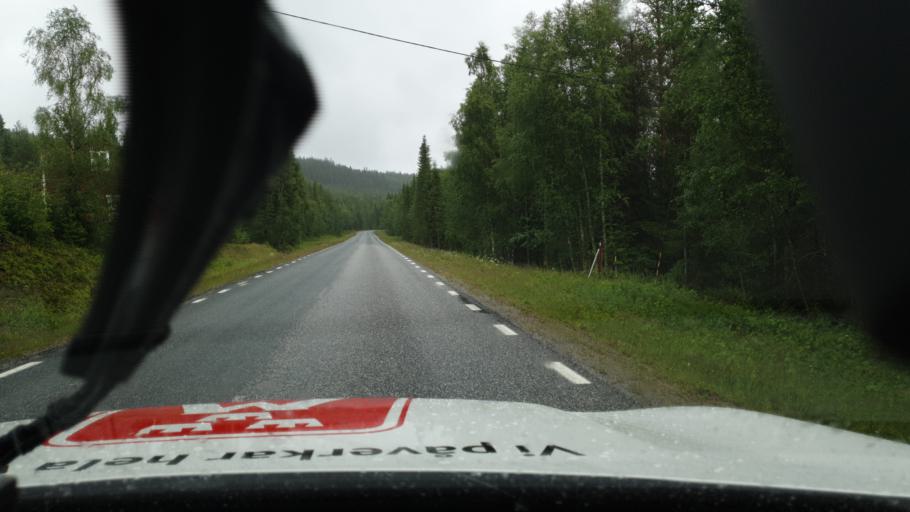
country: SE
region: Vaesterbotten
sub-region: Asele Kommun
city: Insjon
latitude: 64.3469
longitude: 17.7979
